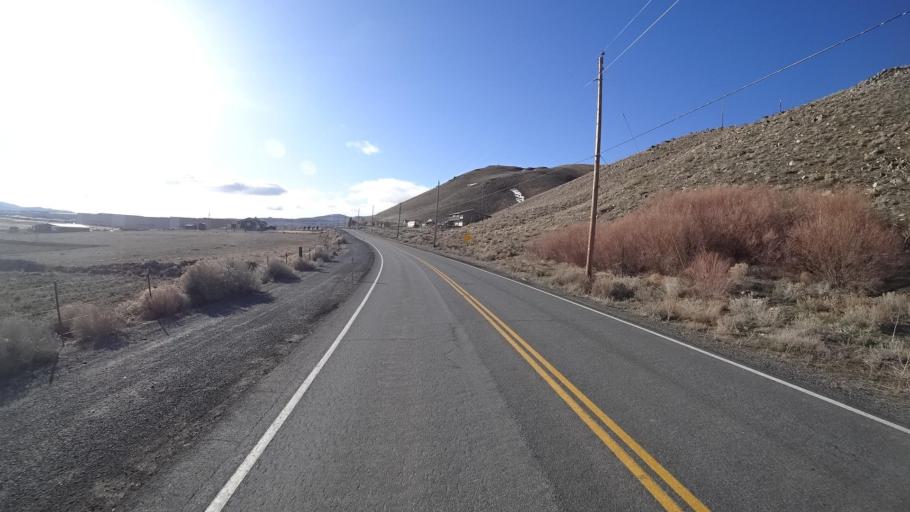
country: US
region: Nevada
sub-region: Washoe County
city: Cold Springs
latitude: 39.6401
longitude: -119.9247
